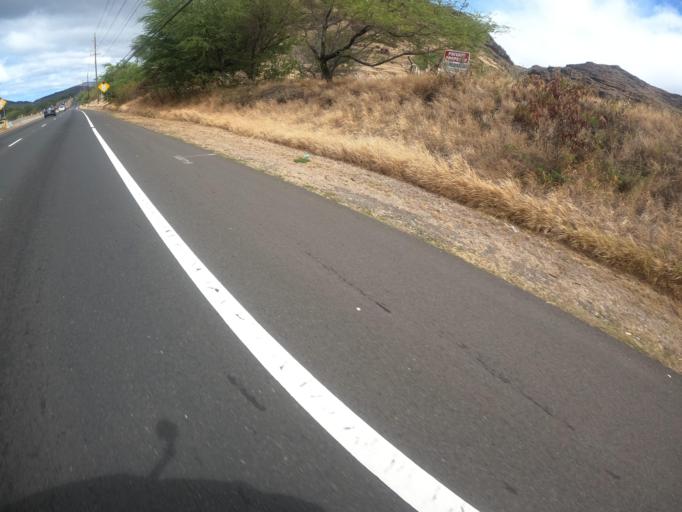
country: US
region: Hawaii
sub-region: Honolulu County
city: Nanakuli
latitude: 21.3631
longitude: -158.1326
